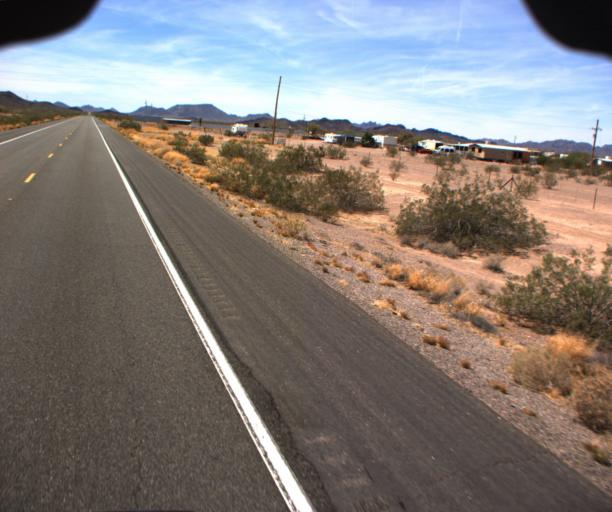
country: US
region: Arizona
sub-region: La Paz County
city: Salome
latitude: 33.6925
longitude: -113.8918
